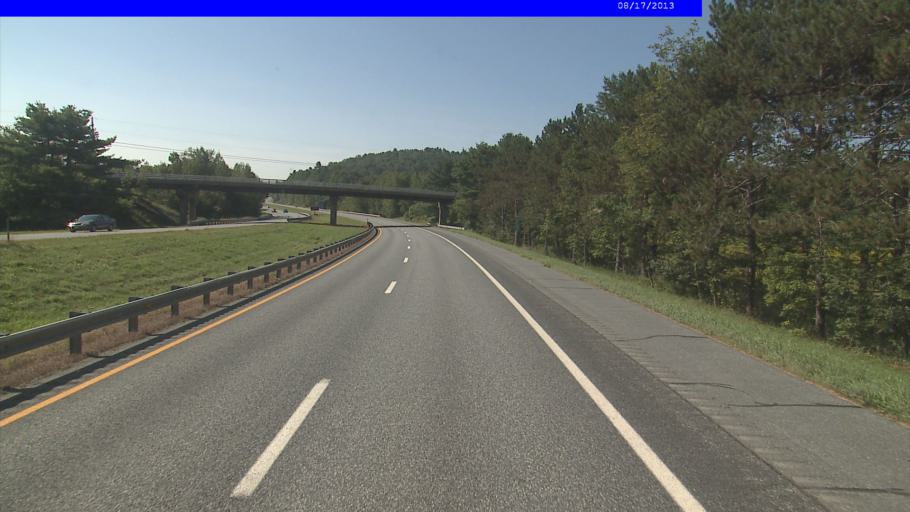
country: US
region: Vermont
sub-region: Windsor County
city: Windsor
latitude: 43.4153
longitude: -72.4155
